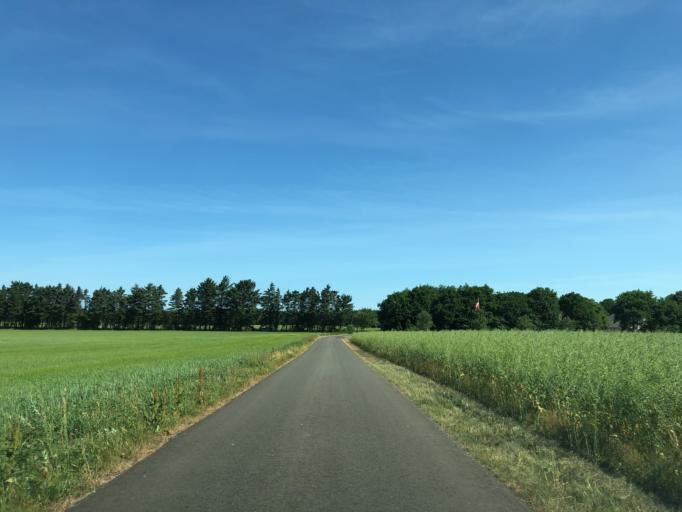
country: DK
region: Central Jutland
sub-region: Struer Kommune
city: Struer
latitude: 56.4276
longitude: 8.4389
